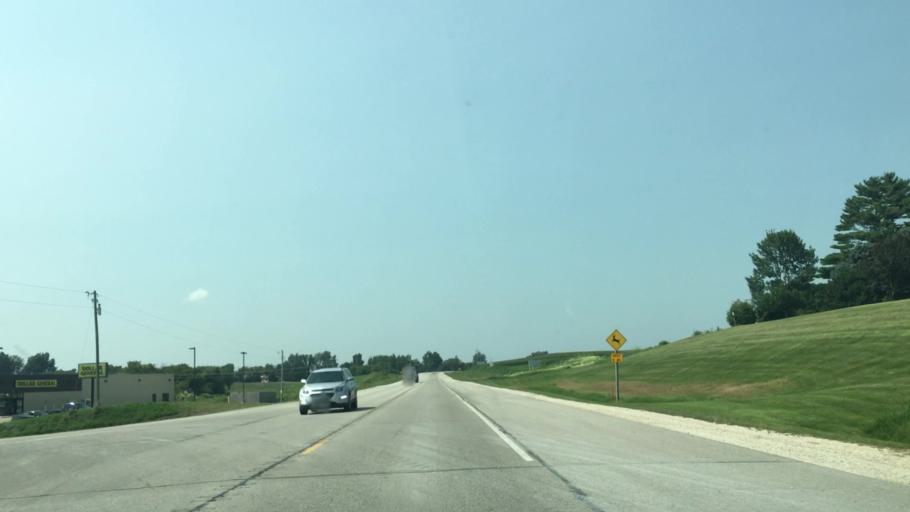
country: US
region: Iowa
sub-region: Winneshiek County
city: Decorah
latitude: 43.1907
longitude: -91.8668
